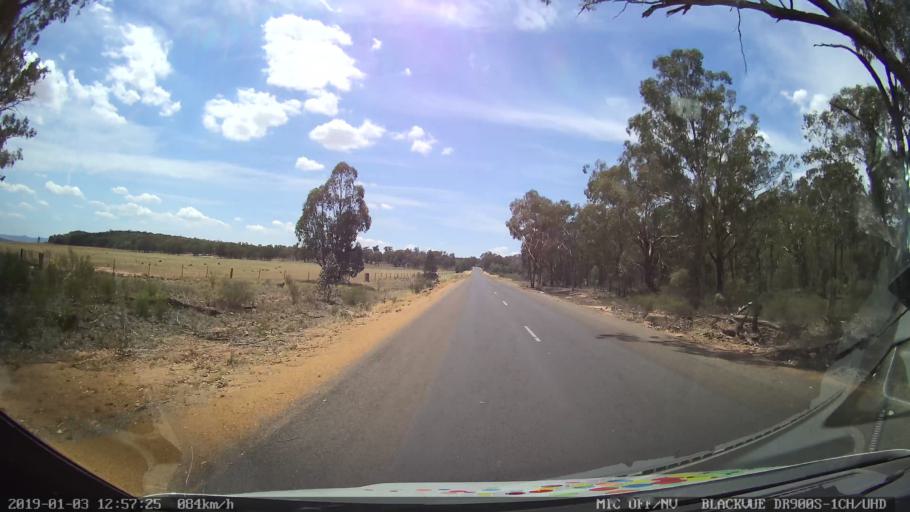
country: AU
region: New South Wales
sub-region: Cabonne
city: Canowindra
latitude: -33.6461
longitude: 148.3612
